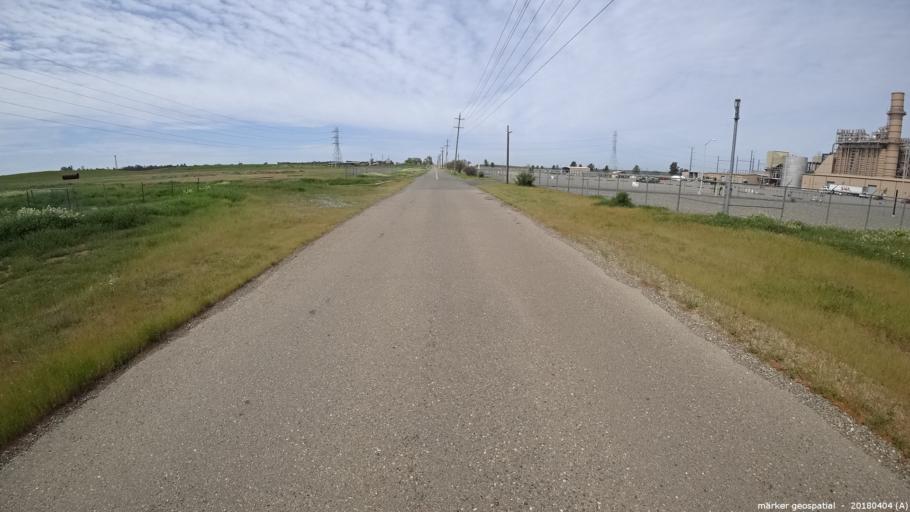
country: US
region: California
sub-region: Sacramento County
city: Clay
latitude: 38.3362
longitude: -121.1223
